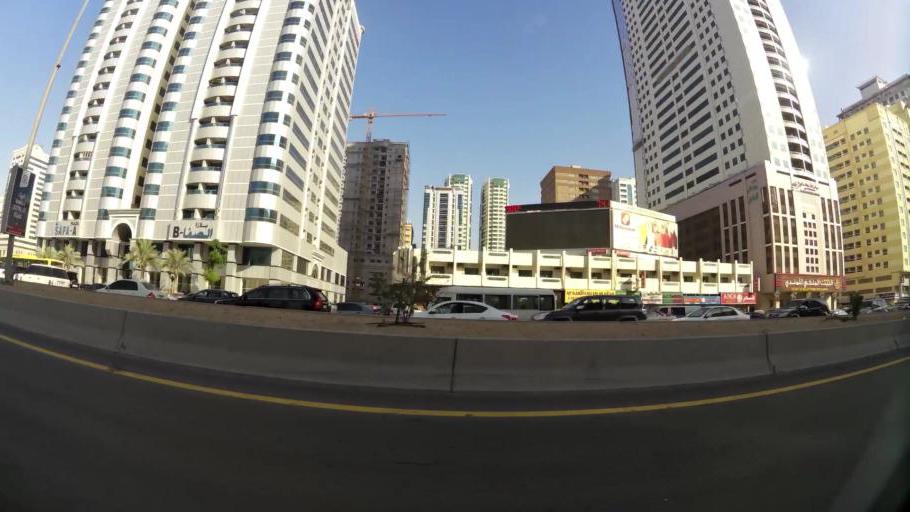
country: AE
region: Ash Shariqah
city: Sharjah
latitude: 25.3084
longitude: 55.3768
